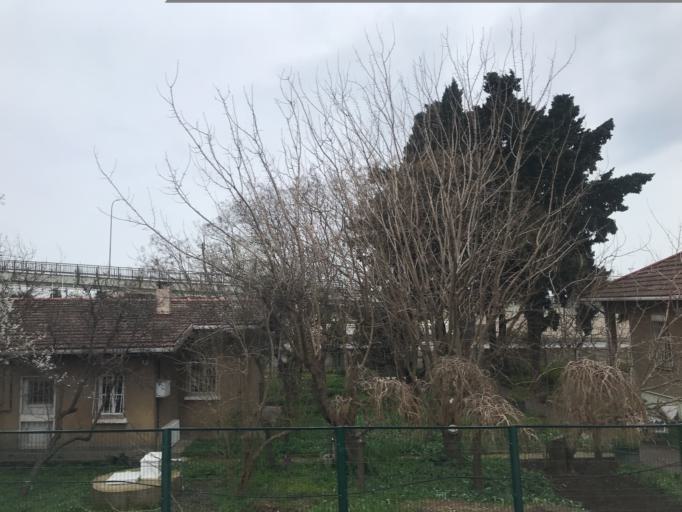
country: TR
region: Istanbul
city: Maltepe
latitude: 40.9345
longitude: 29.1168
